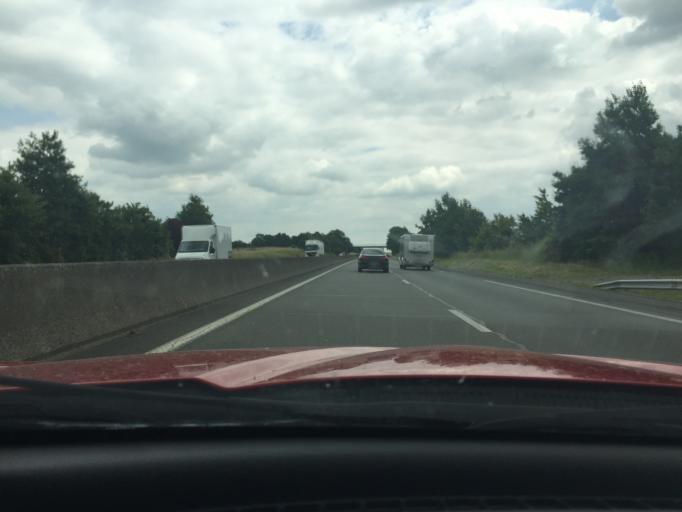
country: FR
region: Picardie
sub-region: Departement de l'Aisne
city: Aulnois-sous-Laon
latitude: 49.6480
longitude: 3.5897
